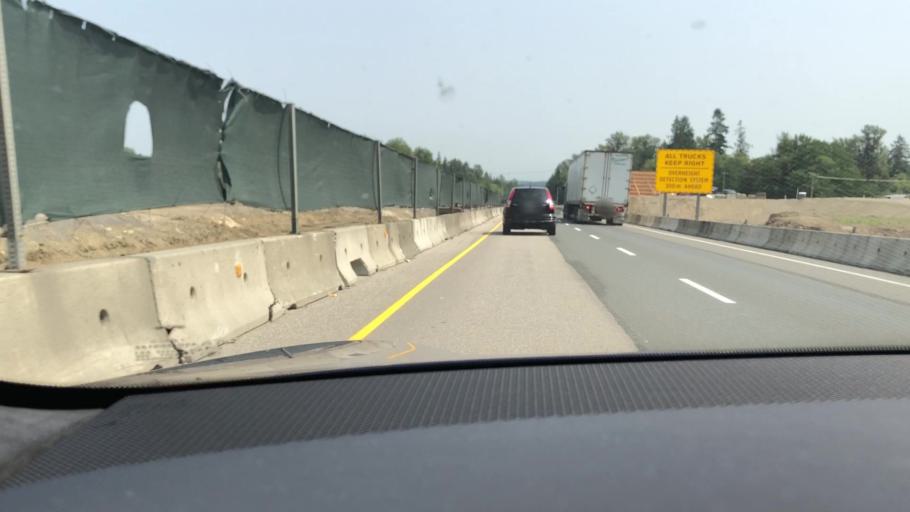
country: CA
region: British Columbia
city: Walnut Grove
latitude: 49.1525
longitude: -122.6259
